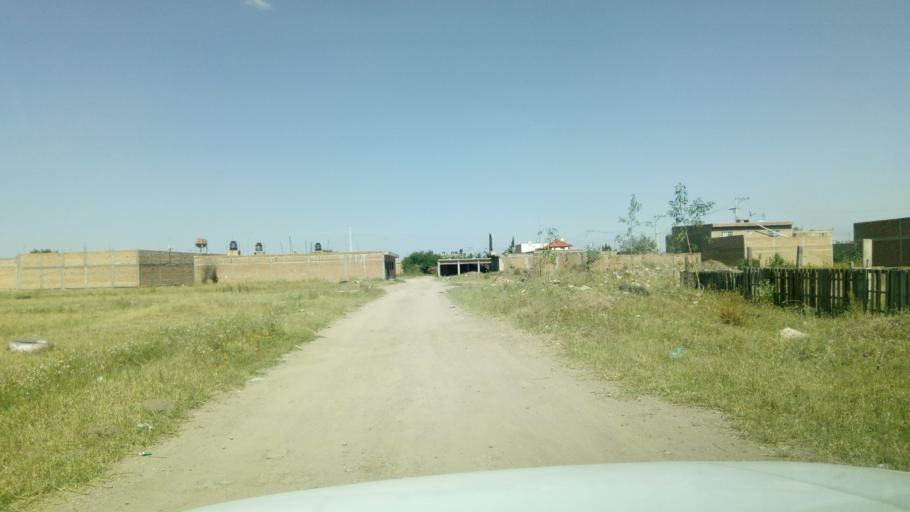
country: MX
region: Durango
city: Victoria de Durango
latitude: 23.9881
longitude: -104.6821
